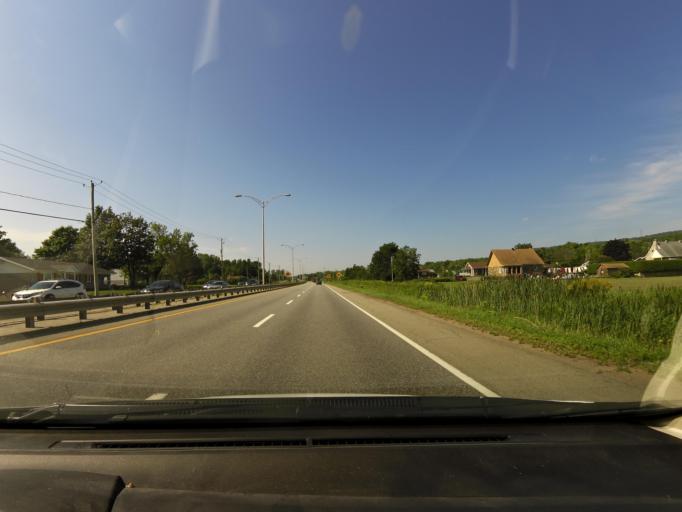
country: CA
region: Quebec
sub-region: Capitale-Nationale
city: Chateau-Richer
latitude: 46.9566
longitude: -71.0378
